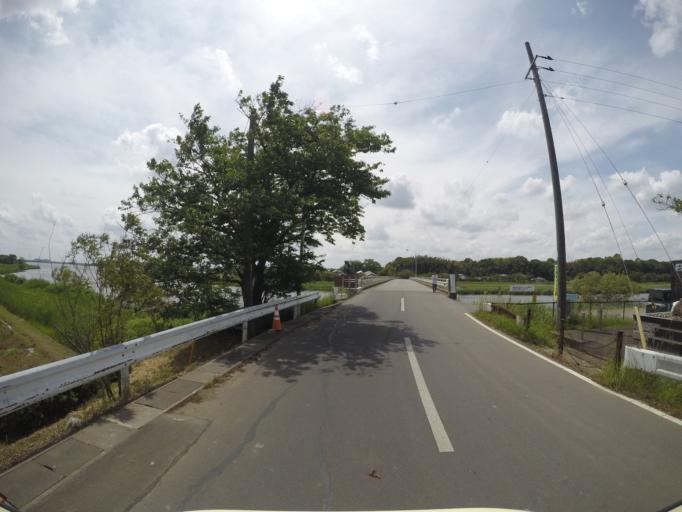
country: JP
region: Ibaraki
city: Ushiku
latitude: 35.9611
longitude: 140.1263
